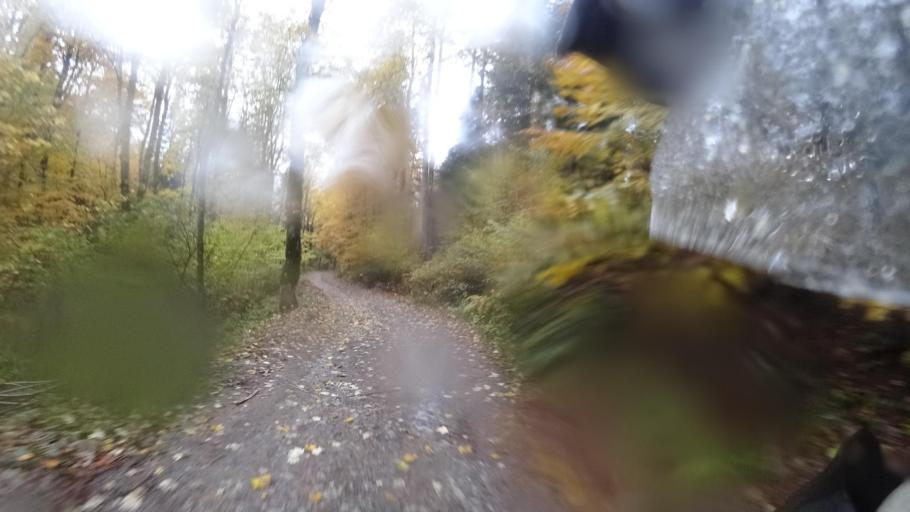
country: HR
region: Primorsko-Goranska
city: Vrbovsko
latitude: 45.3131
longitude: 15.0730
